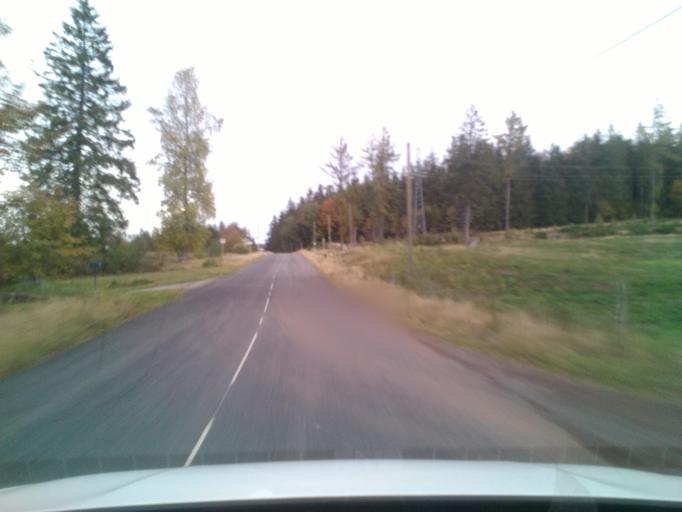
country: FR
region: Lorraine
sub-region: Departement des Vosges
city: Senones
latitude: 48.3814
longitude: 7.0978
